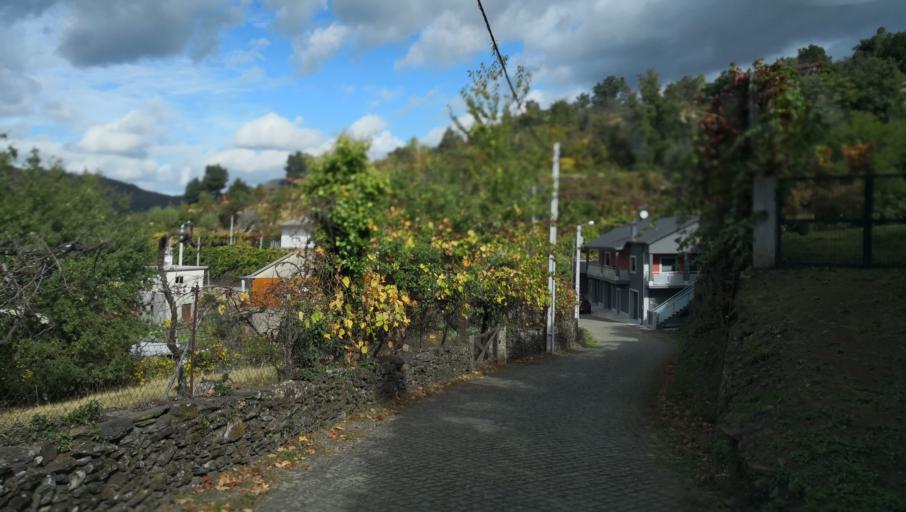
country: PT
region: Vila Real
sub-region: Mondim de Basto
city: Mondim de Basto
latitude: 41.3615
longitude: -7.8871
